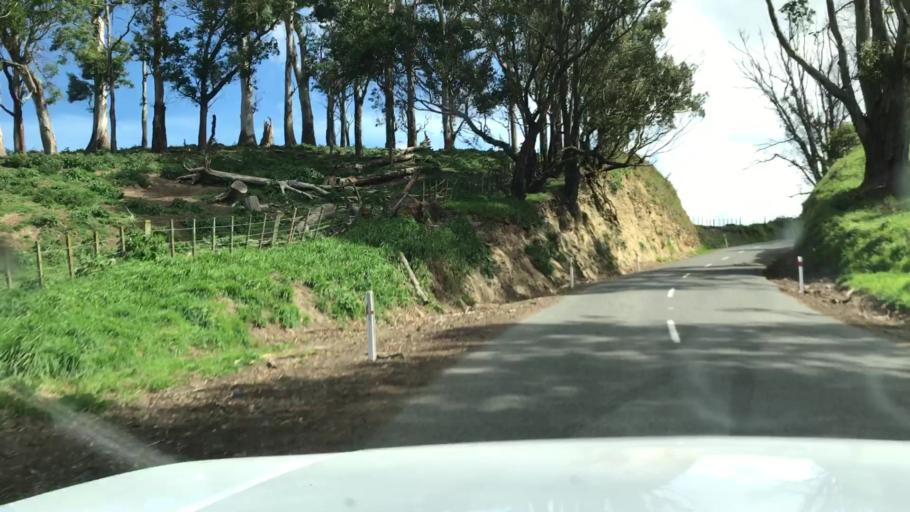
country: NZ
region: Hawke's Bay
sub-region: Hastings District
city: Hastings
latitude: -39.8151
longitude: 176.7512
